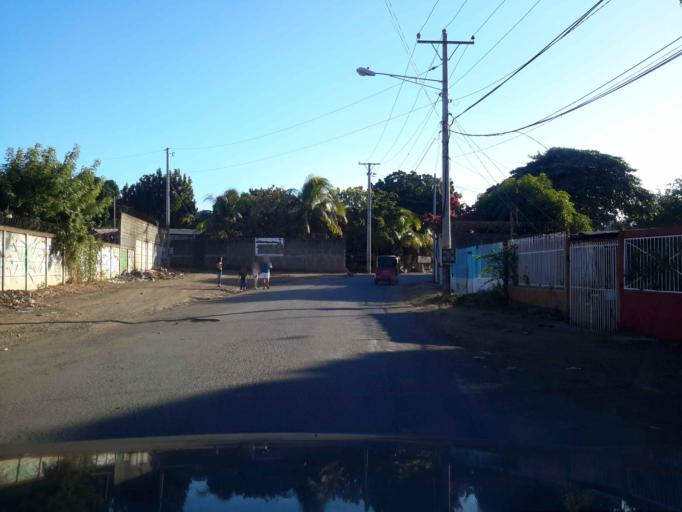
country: NI
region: Managua
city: Managua
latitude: 12.1183
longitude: -86.2891
